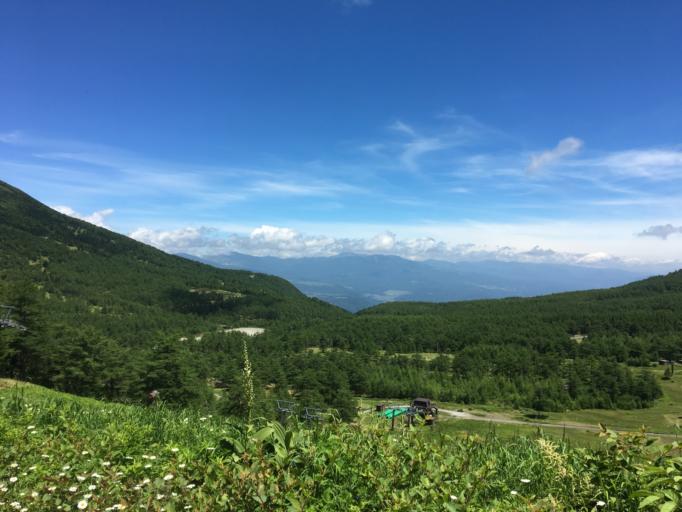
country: JP
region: Nagano
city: Komoro
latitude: 36.4063
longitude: 138.4663
